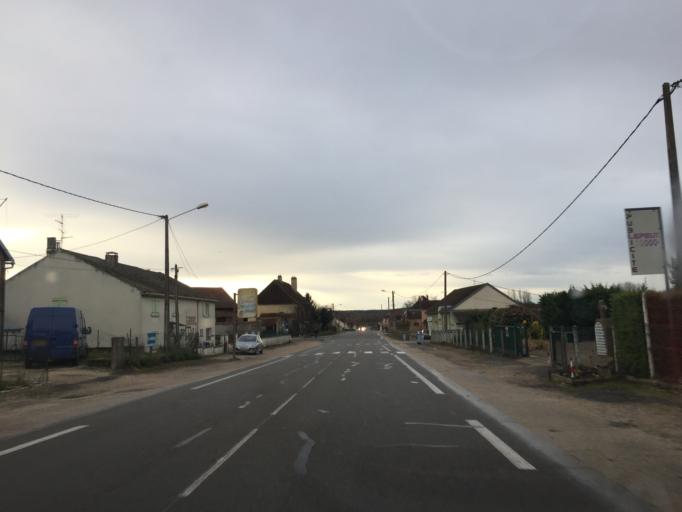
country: FR
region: Franche-Comte
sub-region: Departement du Jura
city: Choisey
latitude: 47.0490
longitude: 5.4945
